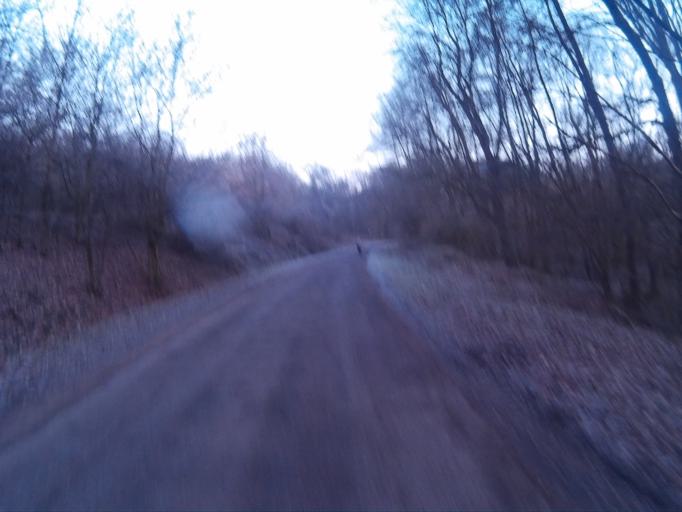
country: HU
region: Borsod-Abauj-Zemplen
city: Putnok
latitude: 48.3155
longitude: 20.4400
